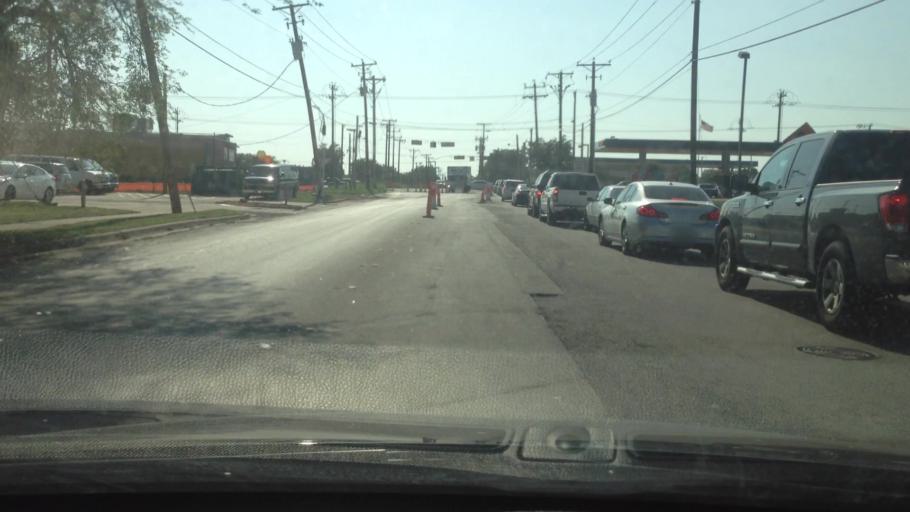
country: US
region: Texas
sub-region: Tarrant County
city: Watauga
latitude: 32.8676
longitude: -97.2364
